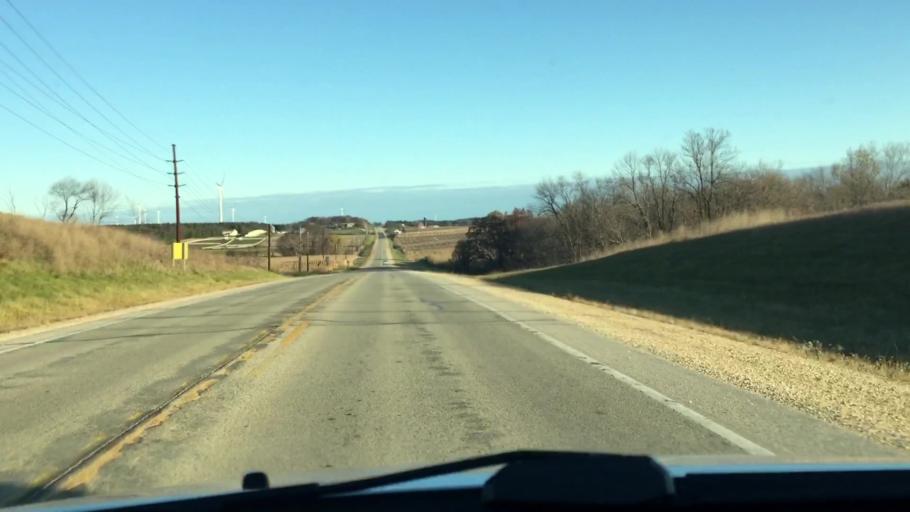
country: US
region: Wisconsin
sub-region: Washington County
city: Hartford
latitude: 43.3863
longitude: -88.4606
